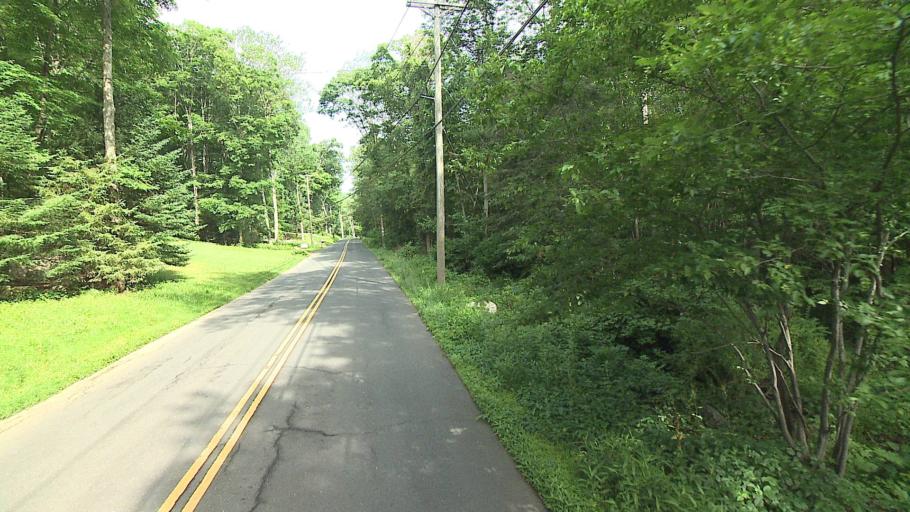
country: US
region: Connecticut
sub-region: New Haven County
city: Southbury
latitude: 41.4387
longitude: -73.1931
